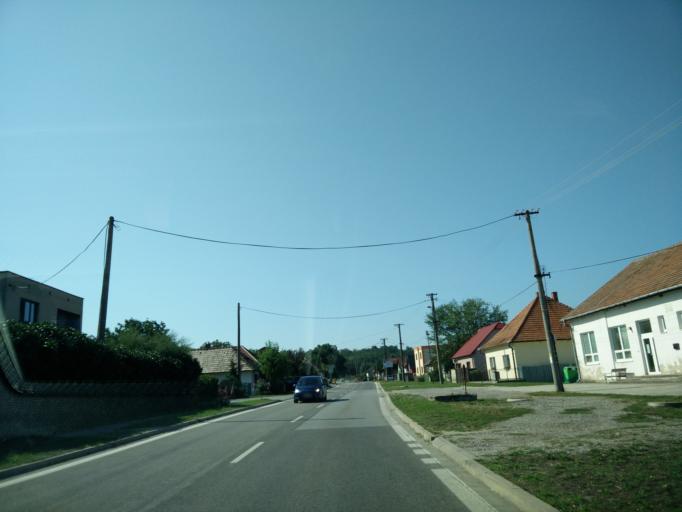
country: SK
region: Nitriansky
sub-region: Okres Nitra
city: Nitra
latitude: 48.4226
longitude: 18.1221
